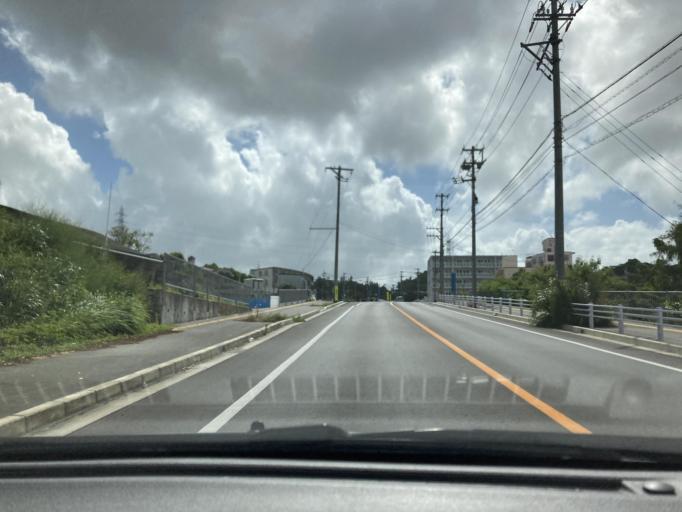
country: JP
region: Okinawa
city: Ginowan
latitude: 26.2590
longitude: 127.7257
